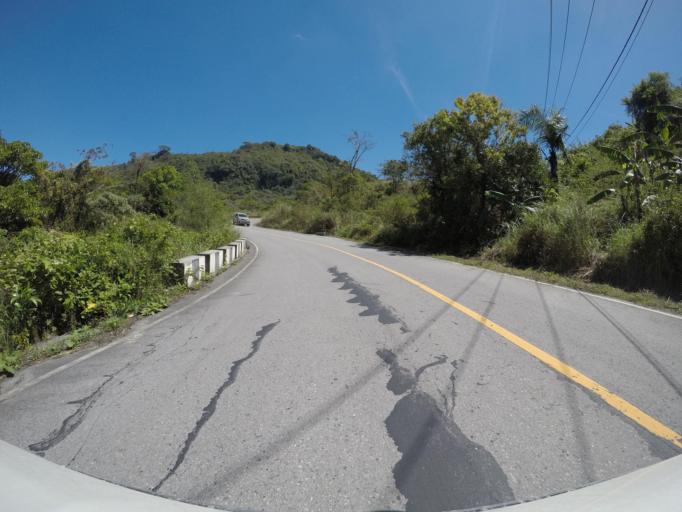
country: TL
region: Manatuto
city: Manatuto
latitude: -8.7666
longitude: 125.9670
